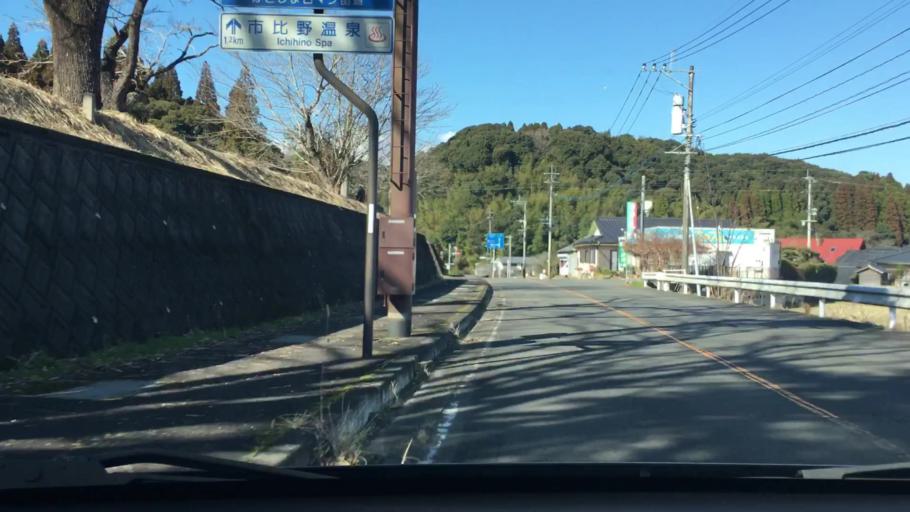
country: JP
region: Kagoshima
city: Satsumasendai
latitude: 31.7775
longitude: 130.4006
